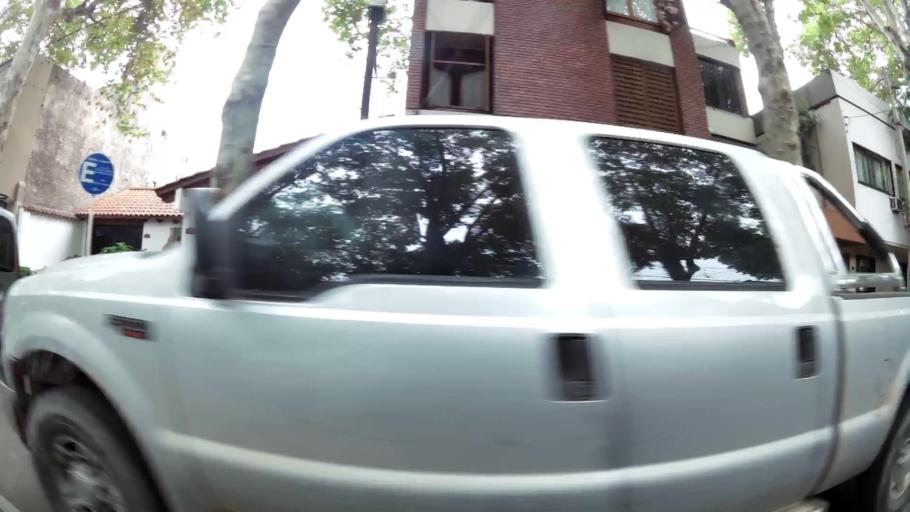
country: AR
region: Mendoza
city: Mendoza
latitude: -32.8872
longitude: -68.8460
